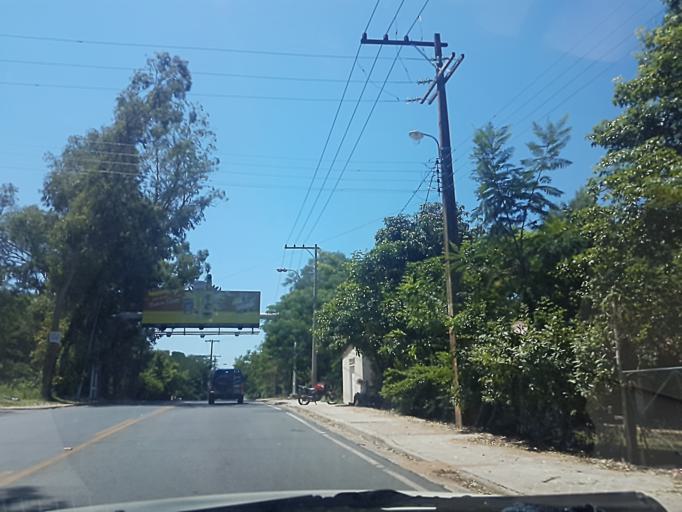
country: PY
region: Cordillera
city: San Bernardino
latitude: -25.2932
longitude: -57.3080
